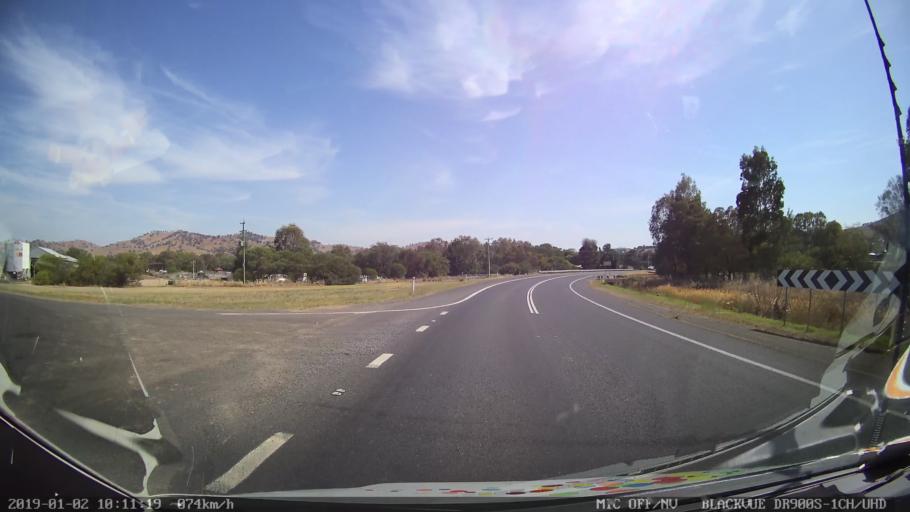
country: AU
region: New South Wales
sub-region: Gundagai
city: Gundagai
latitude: -35.0939
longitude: 148.0918
